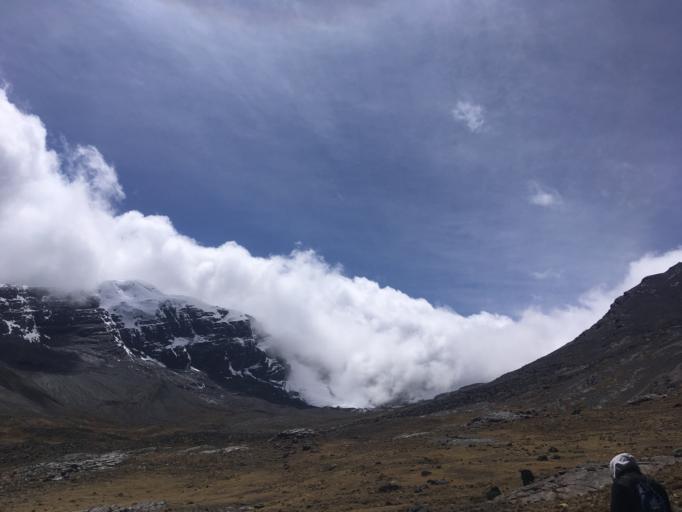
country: BO
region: La Paz
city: La Paz
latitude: -16.3956
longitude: -67.9639
